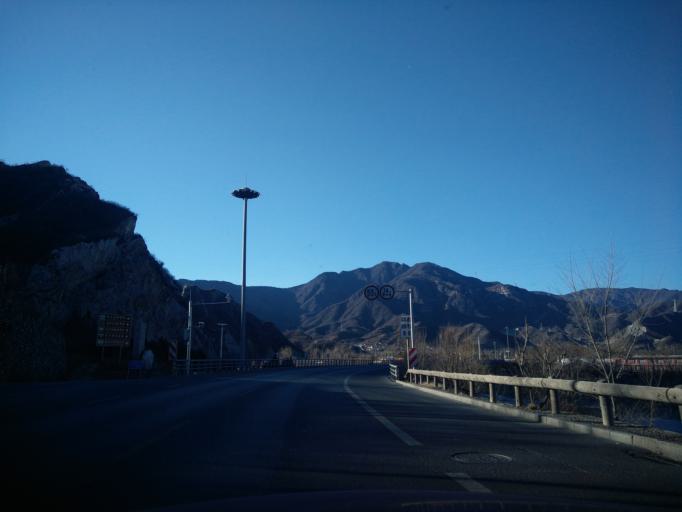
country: CN
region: Beijing
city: Miaofengshan
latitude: 39.9815
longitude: 116.0606
